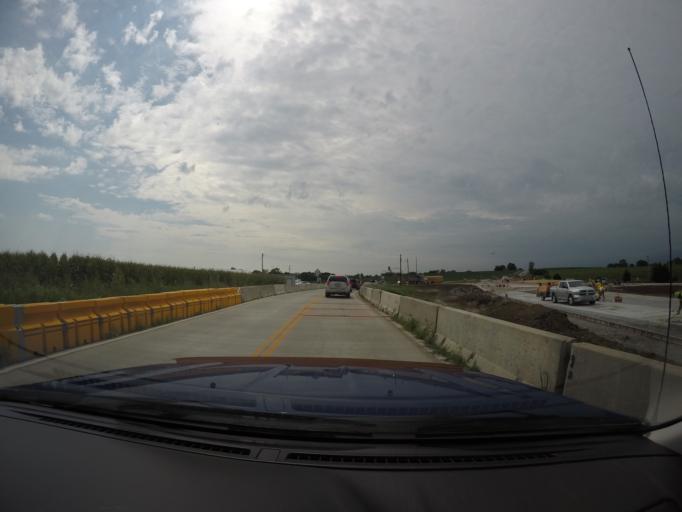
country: US
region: Missouri
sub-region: Lafayette County
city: Lexington
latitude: 39.1223
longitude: -93.9819
